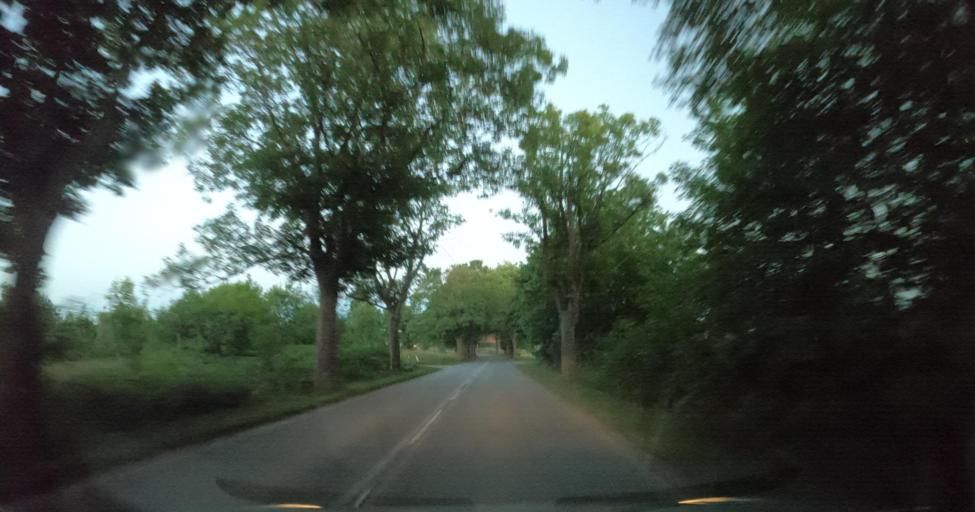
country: PL
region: Pomeranian Voivodeship
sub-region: Powiat wejherowski
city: Szemud
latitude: 54.4728
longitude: 18.2736
